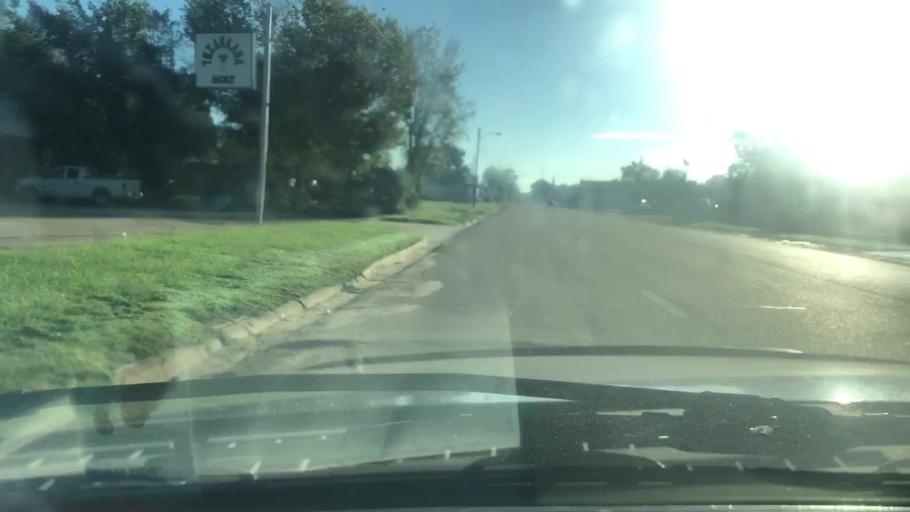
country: US
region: Texas
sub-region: Bowie County
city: Texarkana
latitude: 33.4232
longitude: -94.0660
